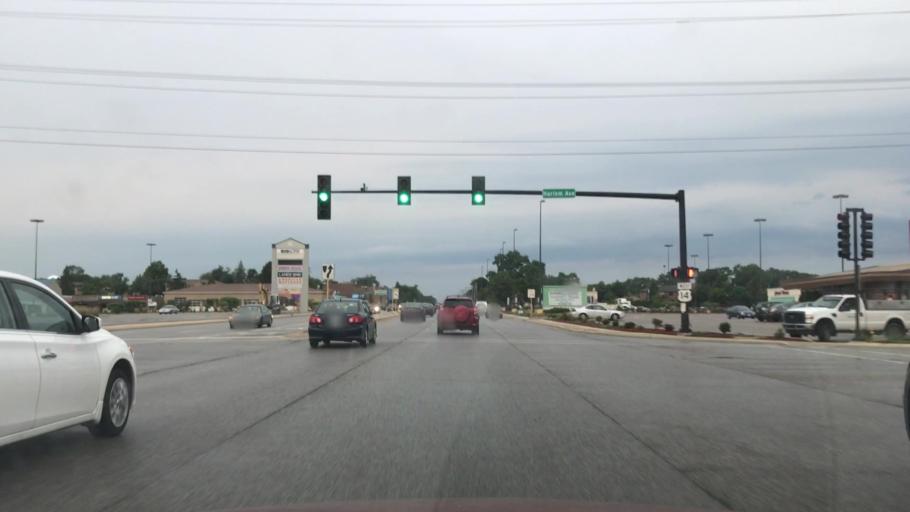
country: US
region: Illinois
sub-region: Cook County
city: Niles
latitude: 42.0409
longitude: -87.8062
